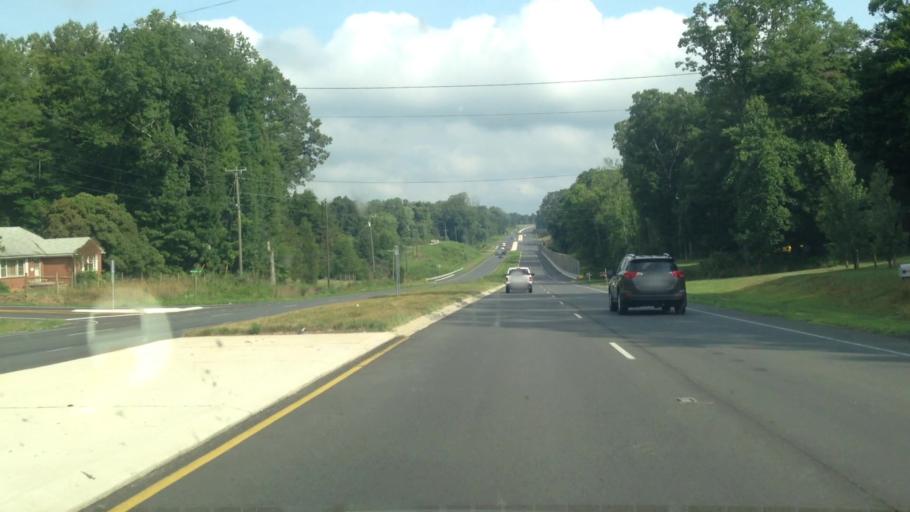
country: US
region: North Carolina
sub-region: Guilford County
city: Summerfield
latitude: 36.1963
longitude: -79.8940
